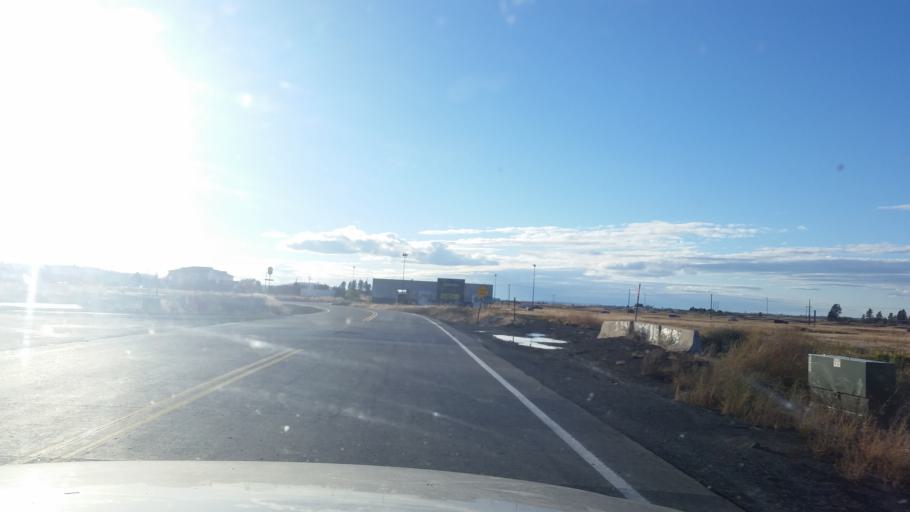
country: US
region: Washington
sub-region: Spokane County
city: Airway Heights
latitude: 47.5875
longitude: -117.5641
